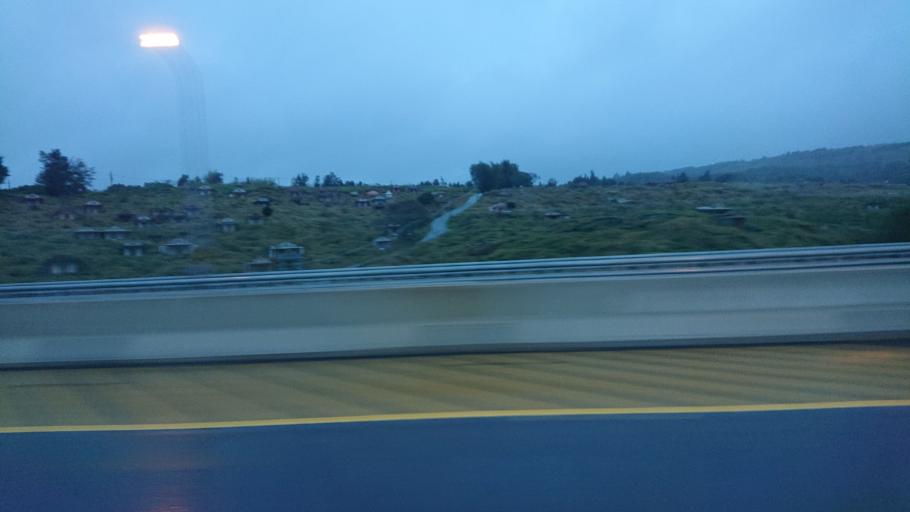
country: TW
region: Taiwan
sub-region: Miaoli
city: Miaoli
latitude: 24.5675
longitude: 120.7144
